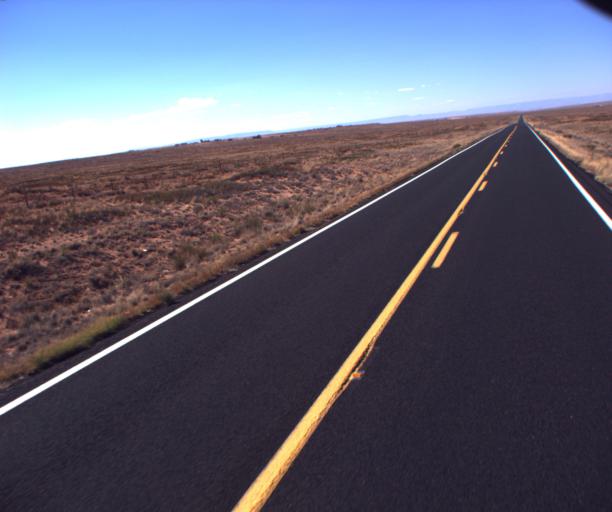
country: US
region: Arizona
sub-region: Coconino County
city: Tuba City
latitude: 36.0119
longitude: -111.0757
